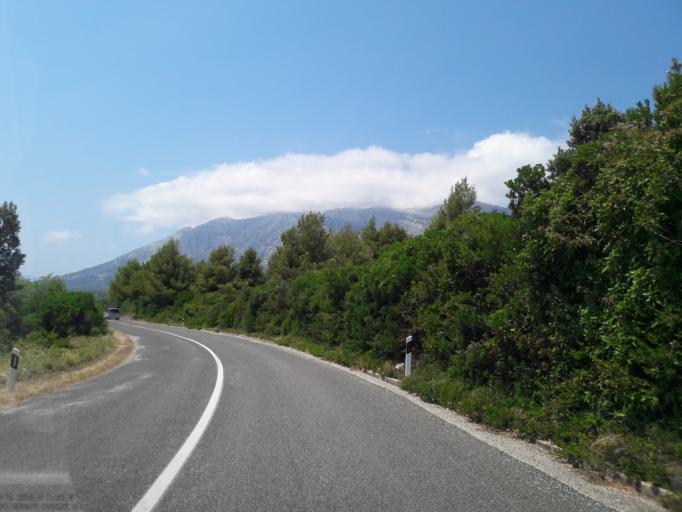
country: HR
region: Dubrovacko-Neretvanska
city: Orebic
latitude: 42.9823
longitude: 17.2168
